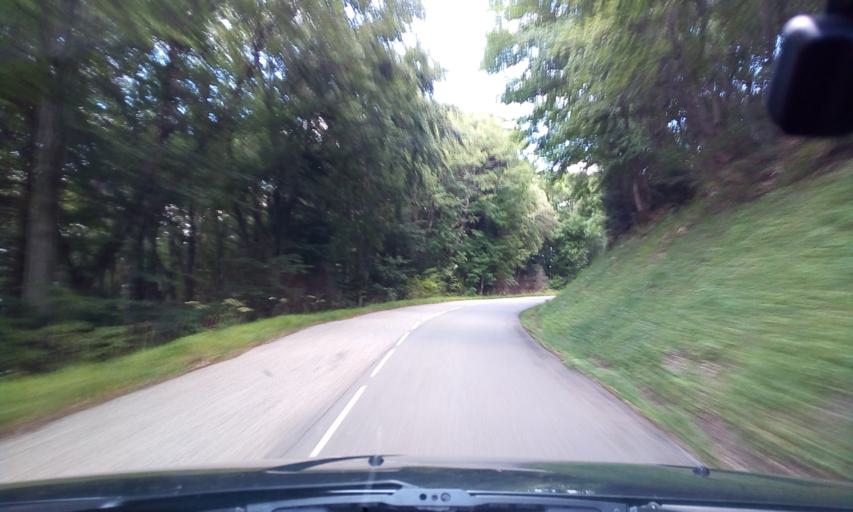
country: FR
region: Rhone-Alpes
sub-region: Departement de l'Isere
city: Chapareillan
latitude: 45.4802
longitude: 5.9506
